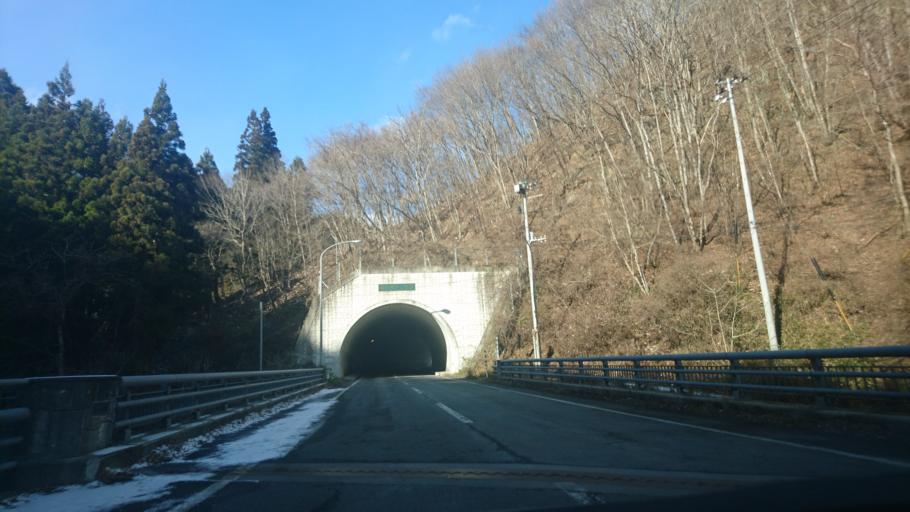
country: JP
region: Iwate
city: Mizusawa
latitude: 39.0872
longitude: 141.3864
